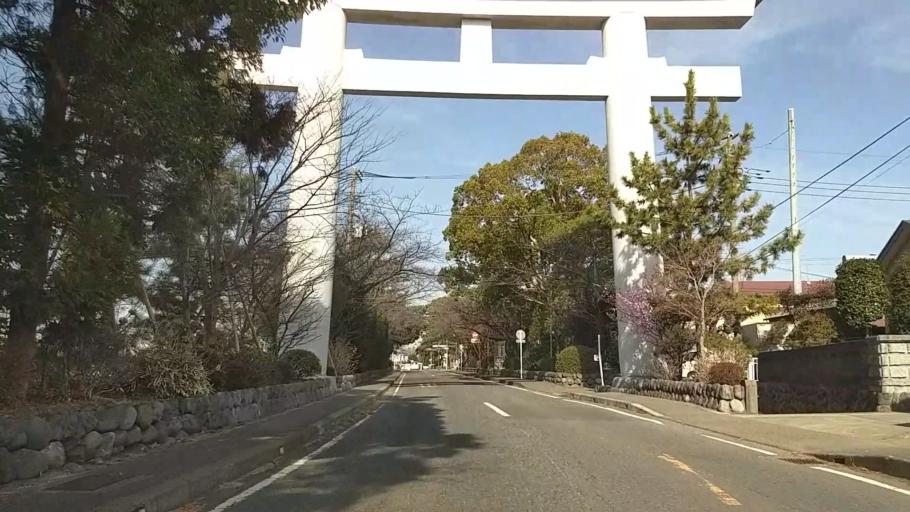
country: JP
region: Kanagawa
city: Chigasaki
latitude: 35.3756
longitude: 139.3808
